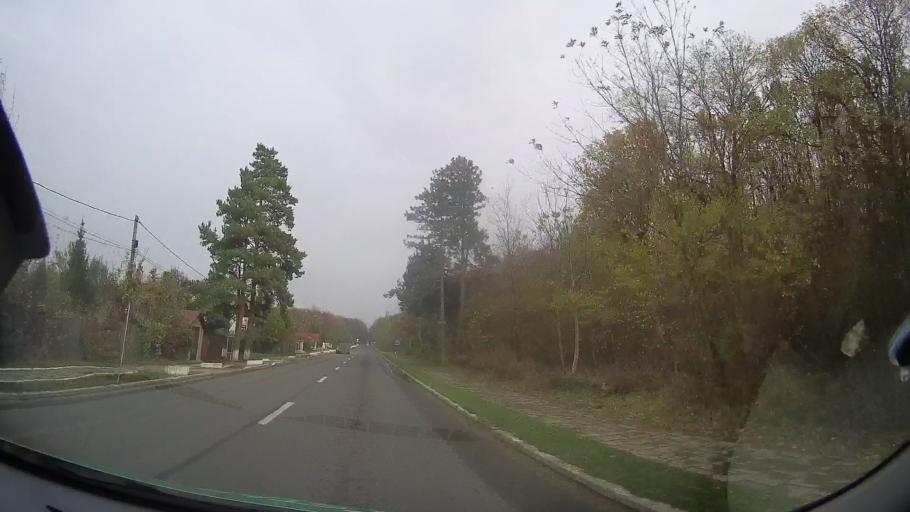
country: RO
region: Ilfov
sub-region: Comuna Snagov
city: Snagov
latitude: 44.7117
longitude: 26.1882
